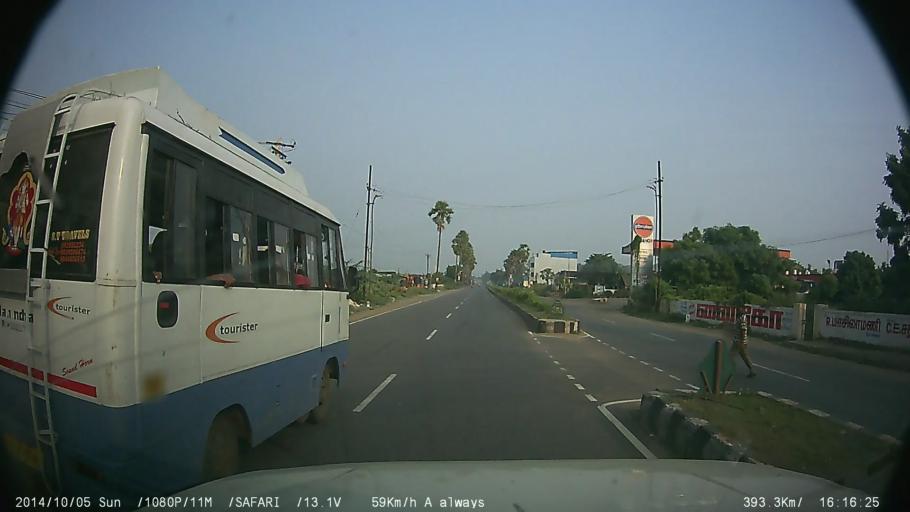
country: IN
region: Tamil Nadu
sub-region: Kancheepuram
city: Vandalur
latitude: 12.8691
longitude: 80.1109
